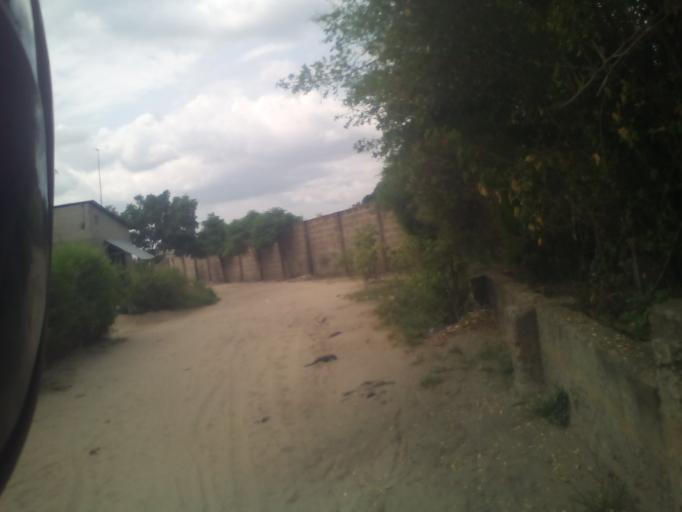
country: TZ
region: Dar es Salaam
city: Dar es Salaam
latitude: -6.8651
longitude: 39.2410
